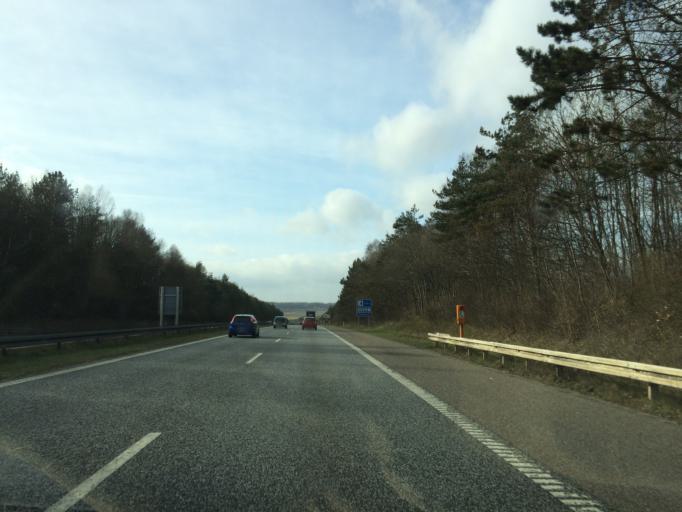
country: DK
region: Central Jutland
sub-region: Randers Kommune
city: Randers
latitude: 56.4395
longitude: 10.0175
